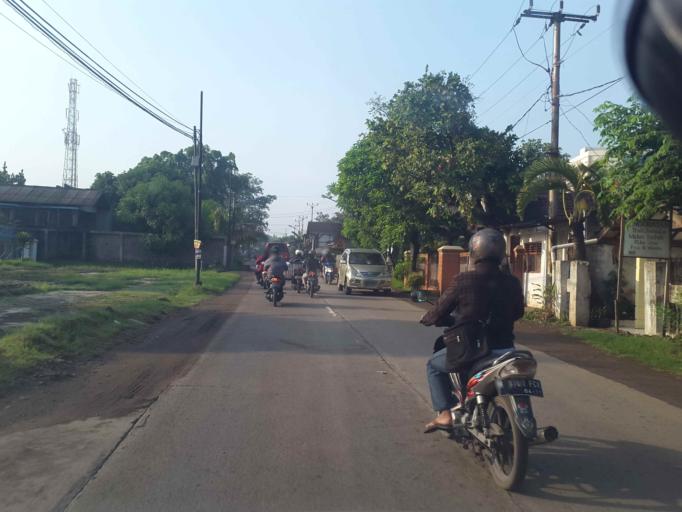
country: ID
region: West Java
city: Cikarang
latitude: -6.2992
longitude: 107.0669
